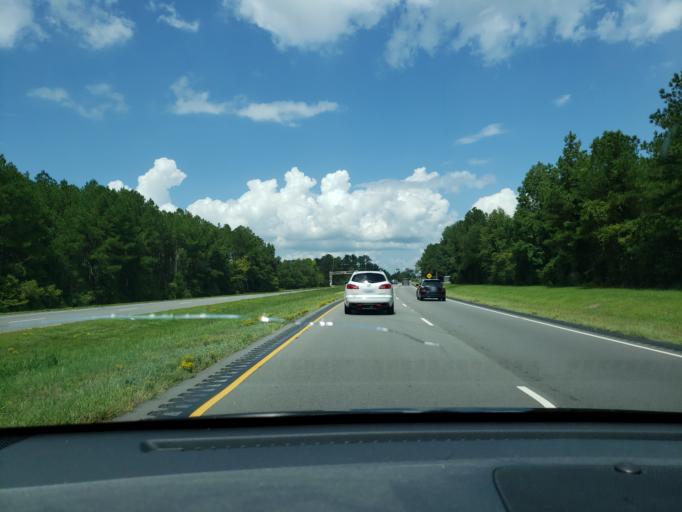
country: US
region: North Carolina
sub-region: Robeson County
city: Saint Pauls
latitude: 34.8384
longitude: -78.8567
